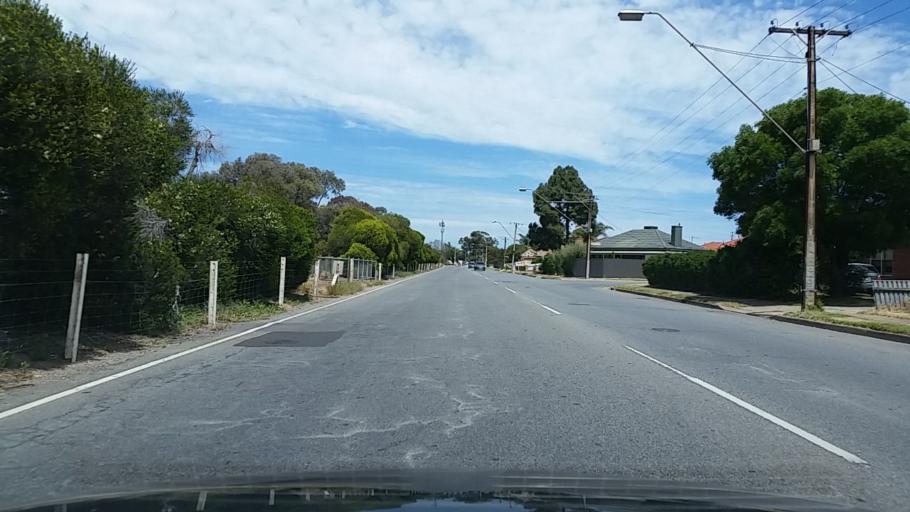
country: AU
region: South Australia
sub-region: Charles Sturt
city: Seaton
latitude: -34.8877
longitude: 138.5173
